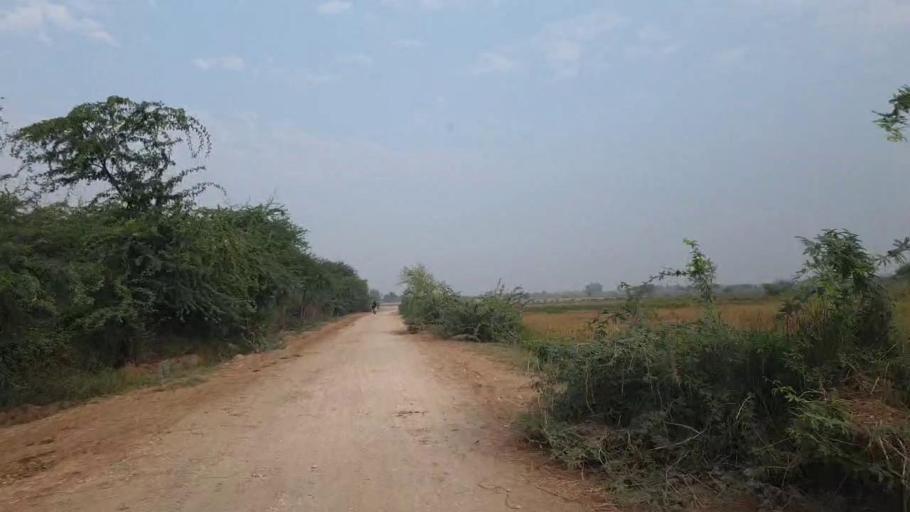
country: PK
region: Sindh
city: Tando Bago
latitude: 24.7878
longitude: 68.8859
